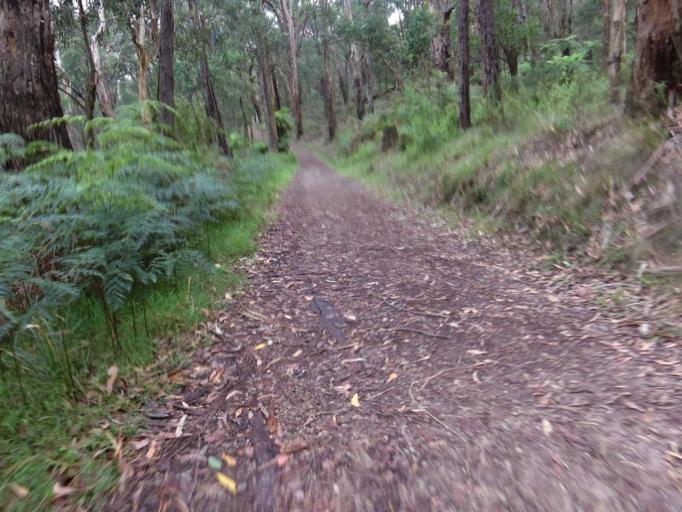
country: AU
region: Victoria
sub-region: Knox
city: The Basin
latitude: -37.8427
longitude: 145.3407
